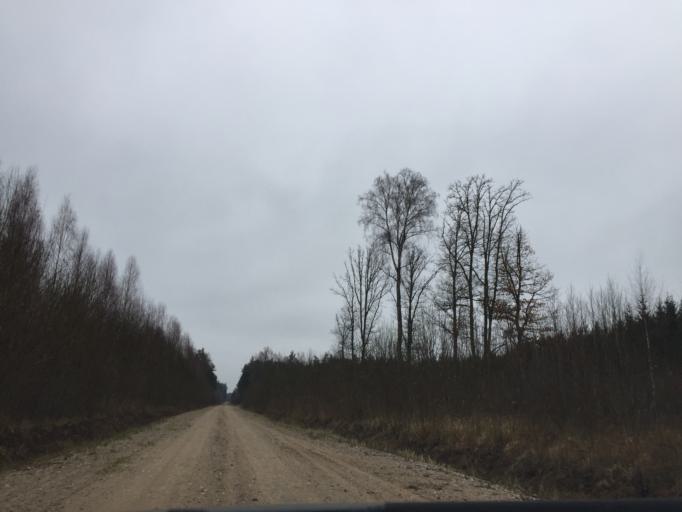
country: LV
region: Limbazu Rajons
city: Limbazi
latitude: 57.4801
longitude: 24.7534
